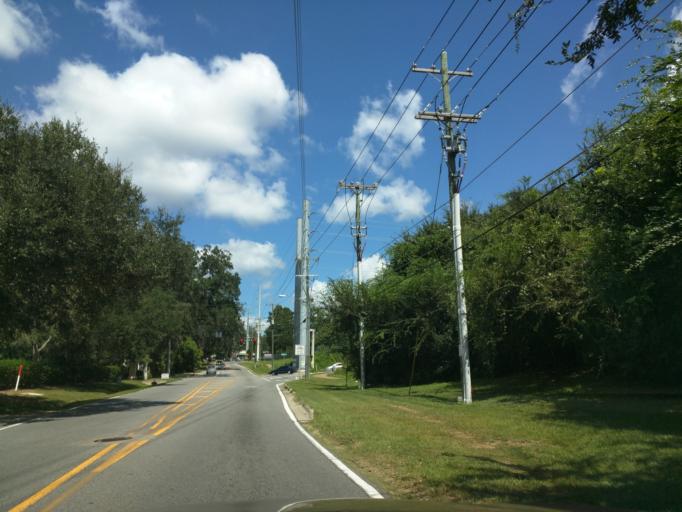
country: US
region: Florida
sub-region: Leon County
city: Tallahassee
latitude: 30.4589
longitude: -84.2224
